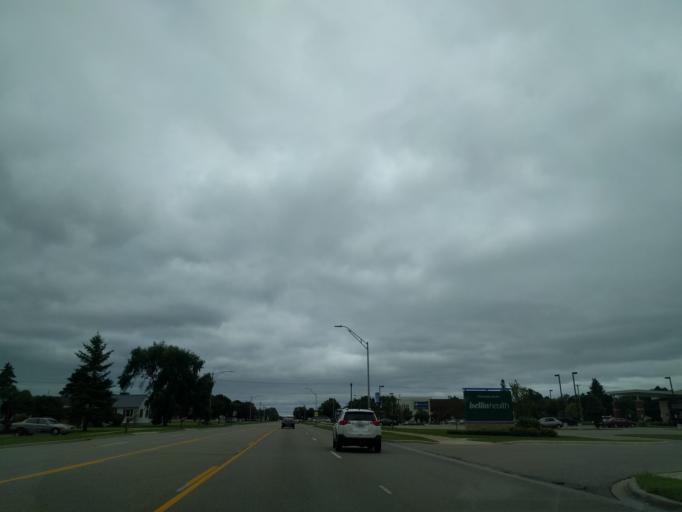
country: US
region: Michigan
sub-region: Delta County
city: Escanaba
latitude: 45.7385
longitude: -87.0799
